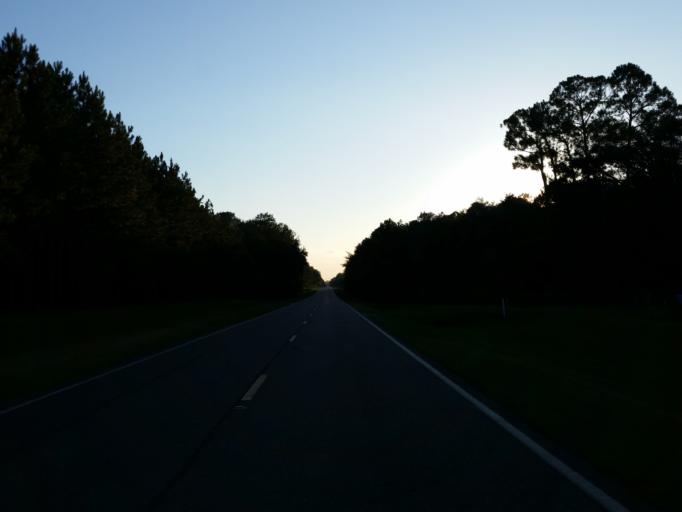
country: US
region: Georgia
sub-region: Berrien County
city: Nashville
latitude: 31.1861
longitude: -83.1594
